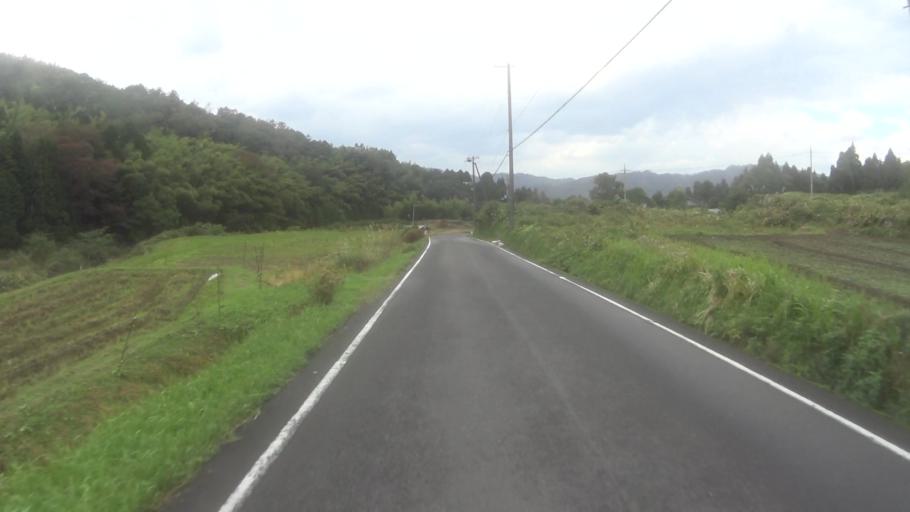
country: JP
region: Kyoto
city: Miyazu
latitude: 35.5158
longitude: 135.1268
